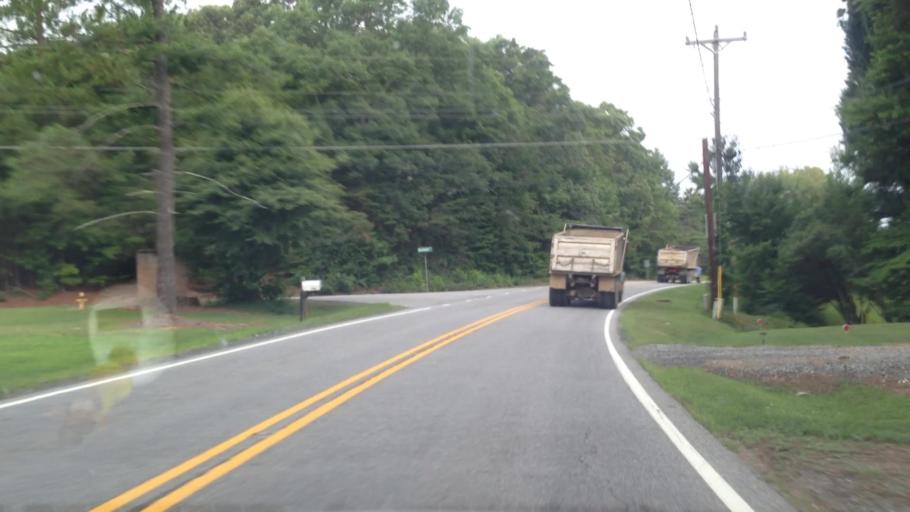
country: US
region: North Carolina
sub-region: Forsyth County
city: Walkertown
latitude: 36.1889
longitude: -80.2131
